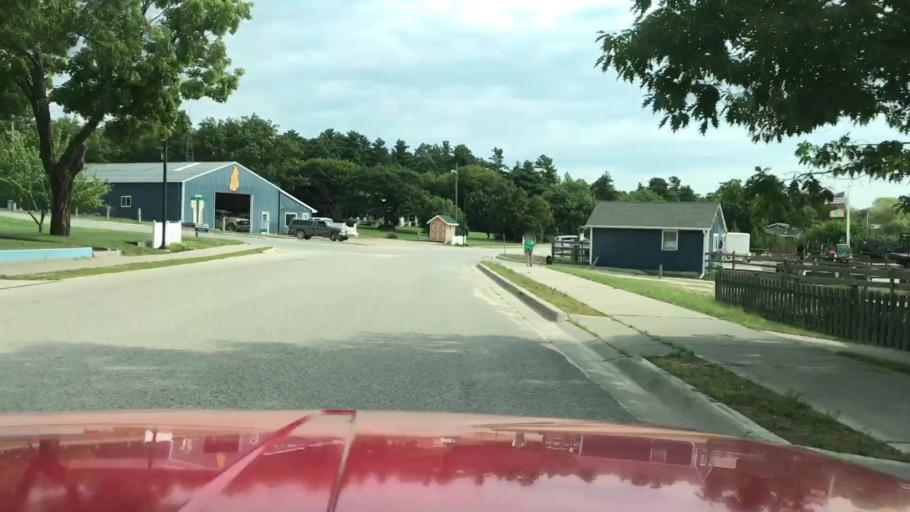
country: US
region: Michigan
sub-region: Charlevoix County
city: Charlevoix
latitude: 45.7498
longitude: -85.5155
